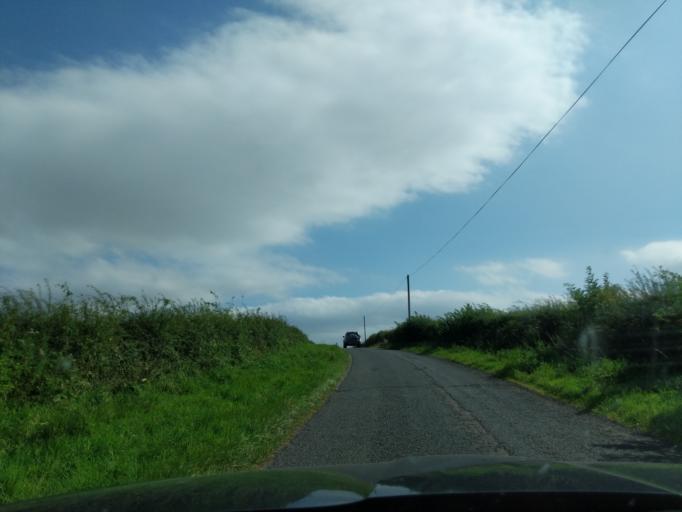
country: GB
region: England
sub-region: Northumberland
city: Ford
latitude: 55.6546
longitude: -2.1483
